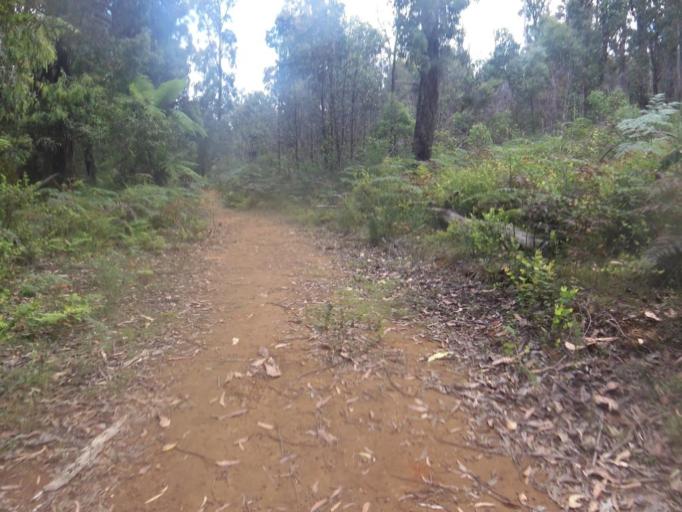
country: AU
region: Victoria
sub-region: Yarra Ranges
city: Millgrove
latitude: -37.5041
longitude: 145.7570
